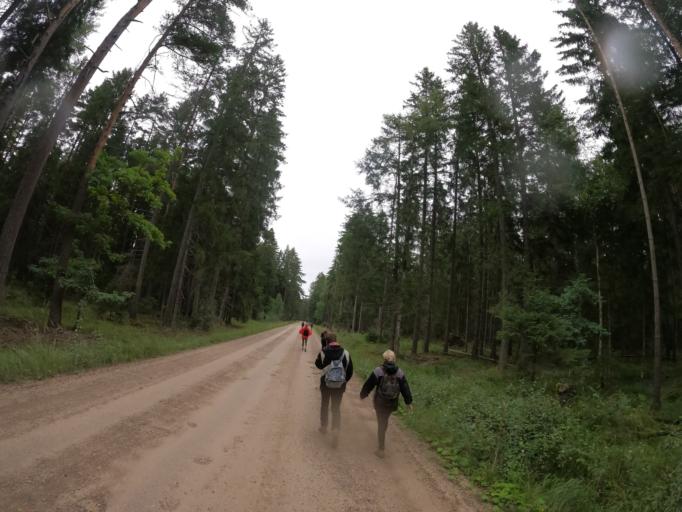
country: LV
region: Kuldigas Rajons
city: Kuldiga
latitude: 56.9938
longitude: 21.9760
